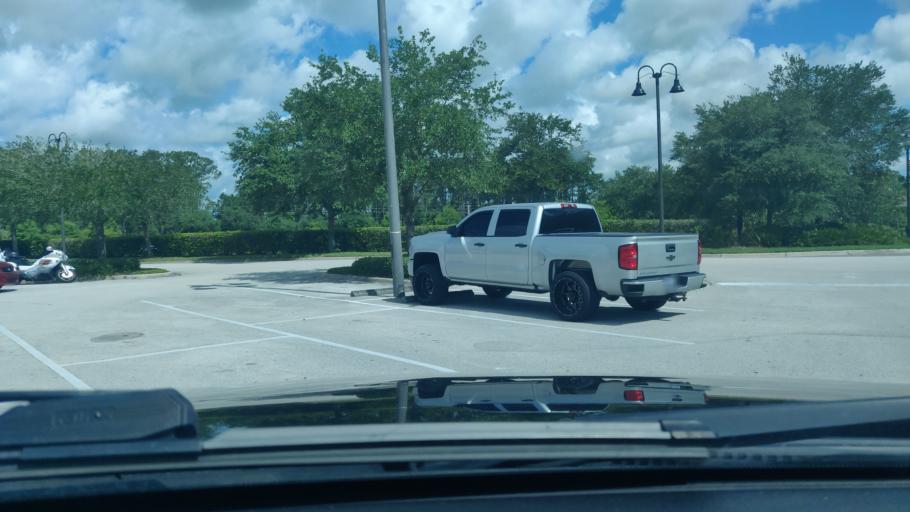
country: US
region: Florida
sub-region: Flagler County
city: Bunnell
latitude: 29.4885
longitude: -81.2202
